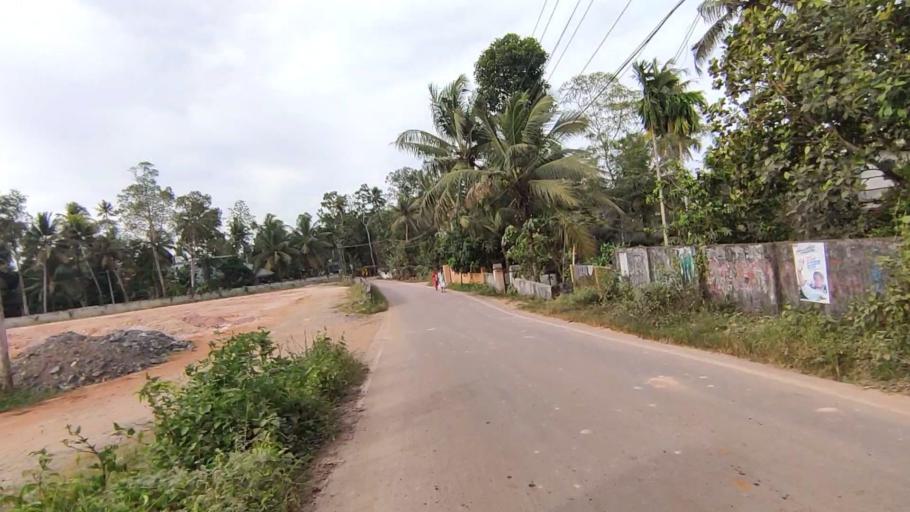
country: IN
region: Kerala
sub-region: Kottayam
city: Kottayam
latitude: 9.5923
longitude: 76.4919
